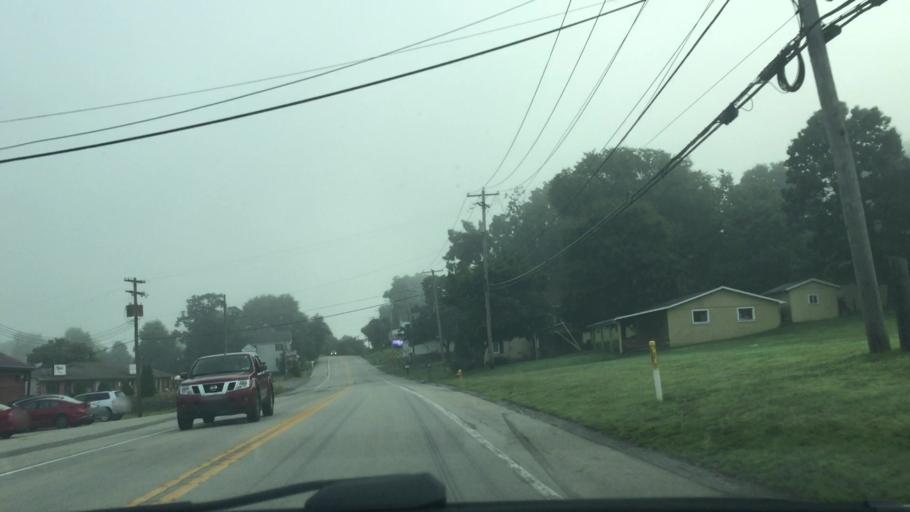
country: US
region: Pennsylvania
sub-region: Washington County
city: Canonsburg
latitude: 40.1933
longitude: -80.1339
